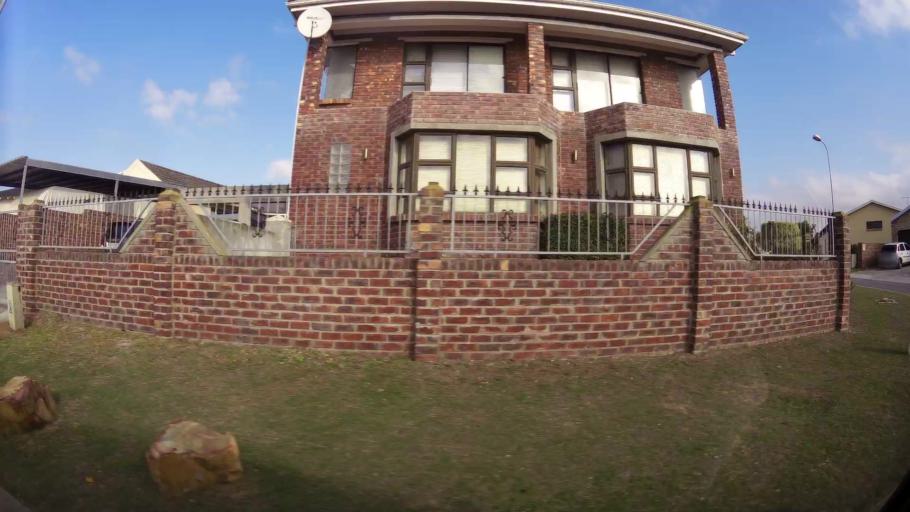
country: ZA
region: Eastern Cape
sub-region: Nelson Mandela Bay Metropolitan Municipality
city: Port Elizabeth
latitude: -33.9250
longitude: 25.5606
